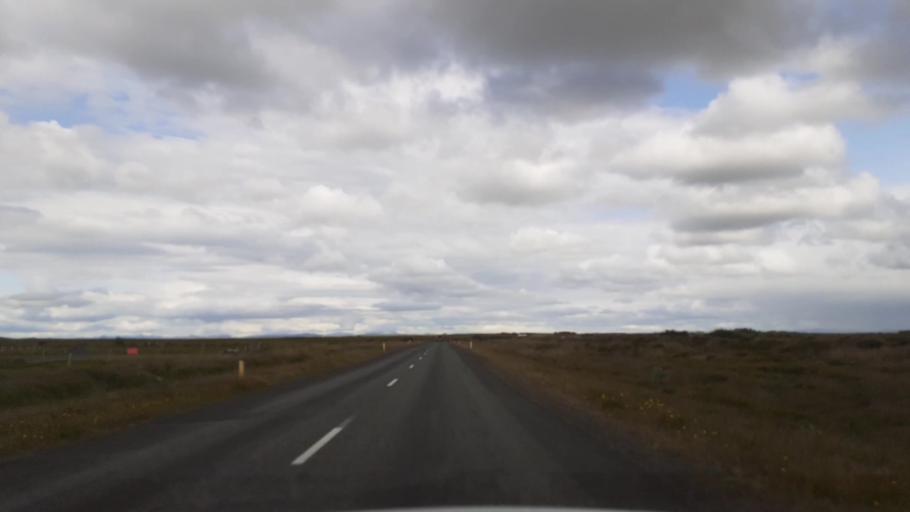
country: IS
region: South
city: Vestmannaeyjar
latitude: 63.8202
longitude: -20.4273
